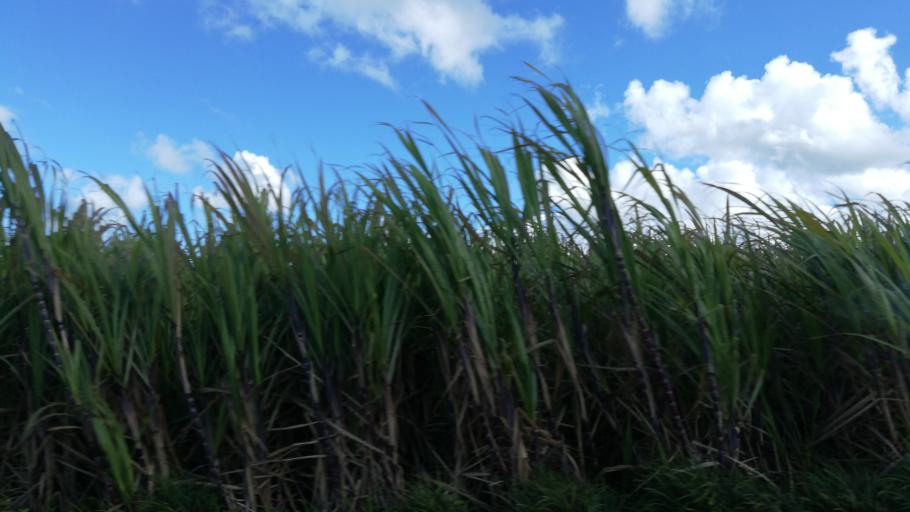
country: MU
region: Moka
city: Quartier Militaire
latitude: -20.2298
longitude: 57.5754
